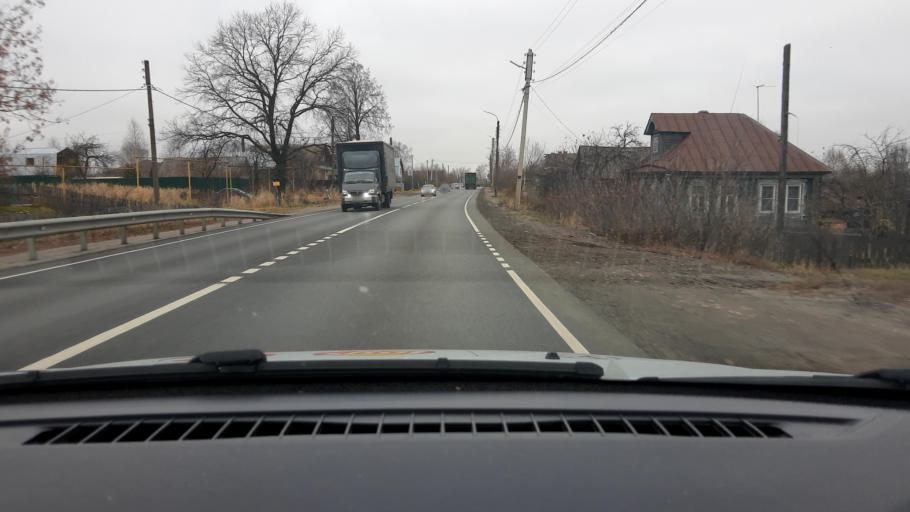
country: RU
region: Nizjnij Novgorod
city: Gidrotorf
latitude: 56.5348
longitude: 43.5394
